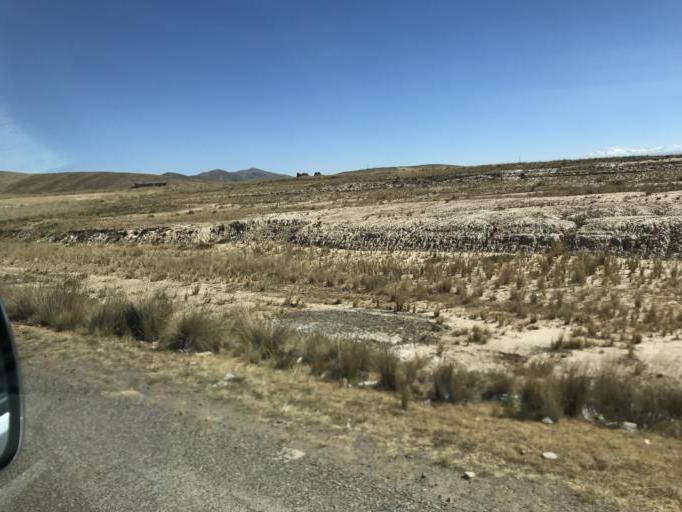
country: BO
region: La Paz
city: La Paz
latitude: -16.5312
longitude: -68.3946
